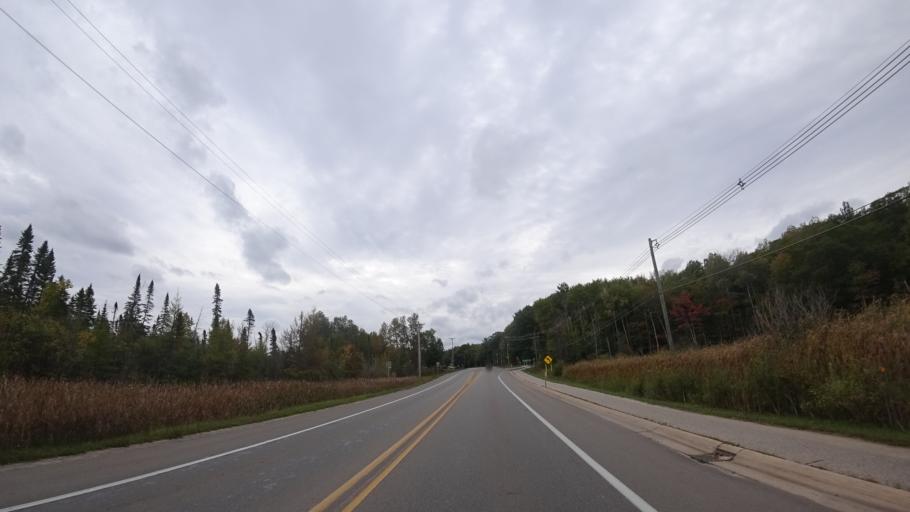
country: US
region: Michigan
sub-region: Emmet County
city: Petoskey
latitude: 45.4161
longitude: -84.9045
